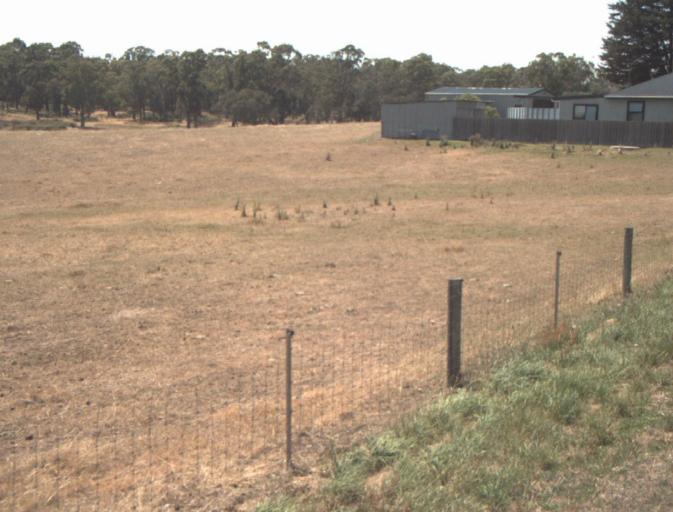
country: AU
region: Tasmania
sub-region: Northern Midlands
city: Perth
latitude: -41.5028
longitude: 147.1973
